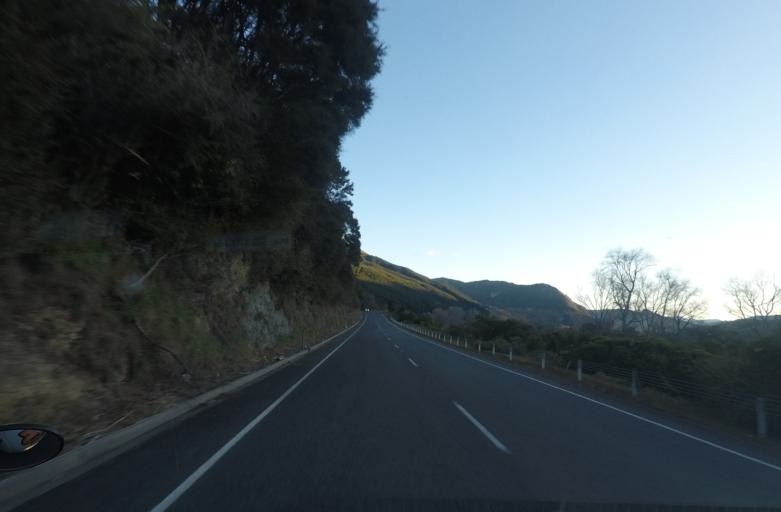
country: NZ
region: Marlborough
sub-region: Marlborough District
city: Picton
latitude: -41.2765
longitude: 173.7305
